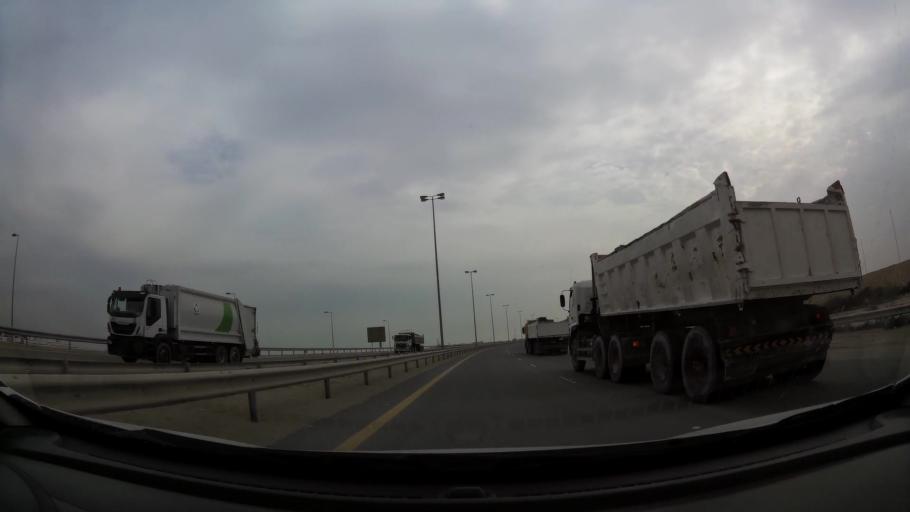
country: BH
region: Northern
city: Sitrah
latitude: 26.0723
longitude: 50.6150
